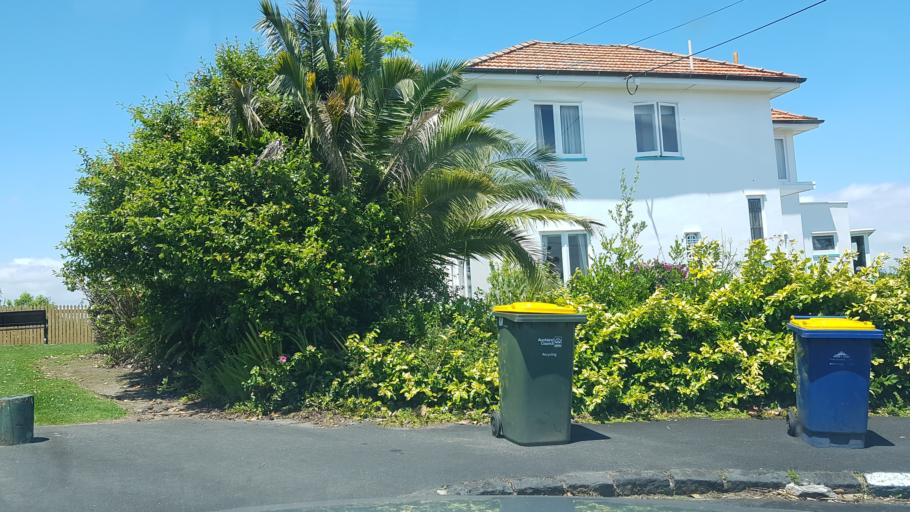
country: NZ
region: Auckland
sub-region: Auckland
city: North Shore
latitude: -36.8290
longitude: 174.7734
